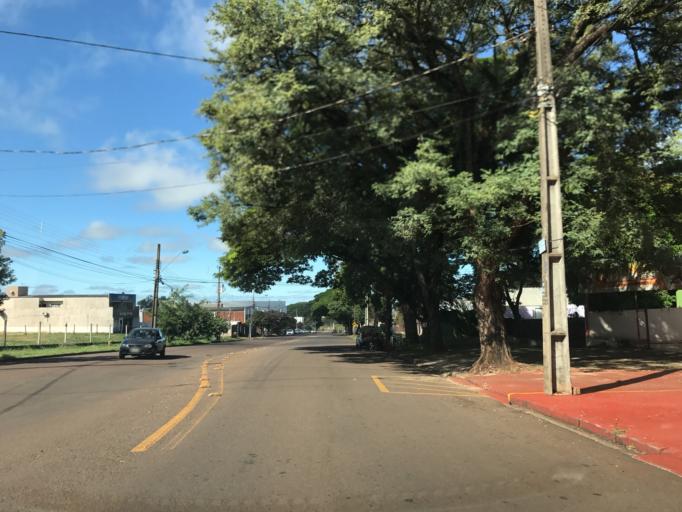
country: BR
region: Parana
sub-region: Maringa
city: Maringa
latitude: -23.4506
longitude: -51.9540
